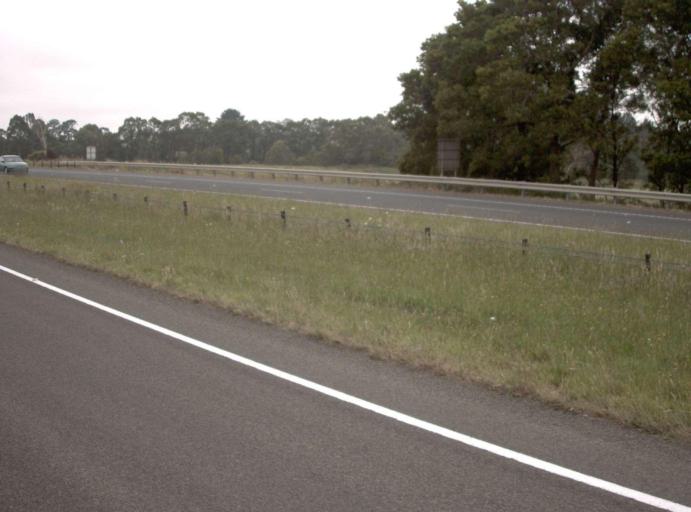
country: AU
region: Victoria
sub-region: Baw Baw
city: Warragul
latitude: -38.1446
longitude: 145.8846
